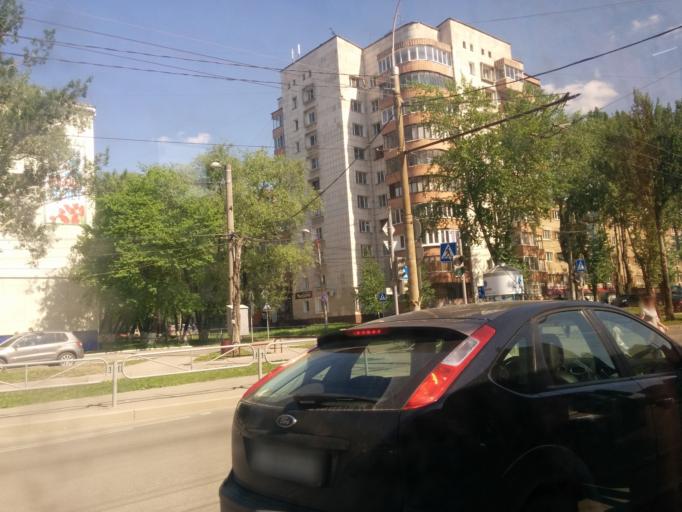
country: RU
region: Perm
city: Perm
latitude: 58.0105
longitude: 56.2809
